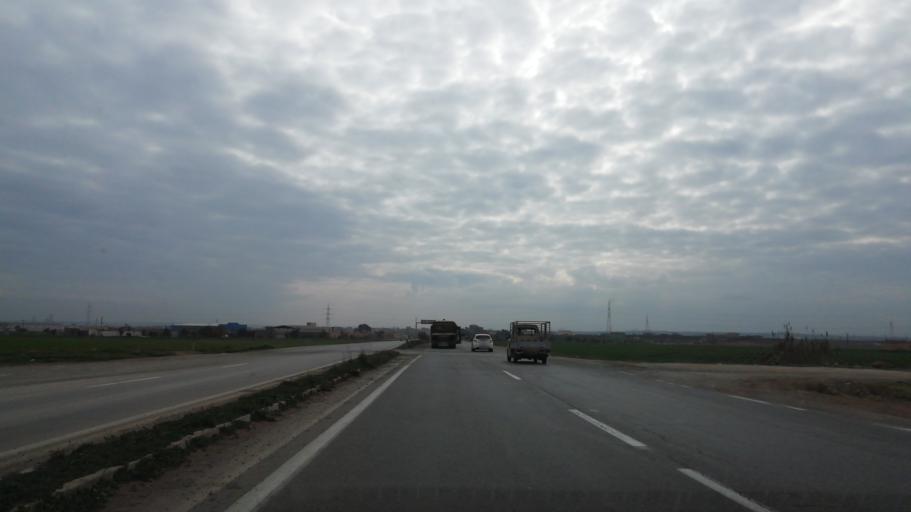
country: DZ
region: Oran
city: Ain el Bya
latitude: 35.7965
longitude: -0.3444
